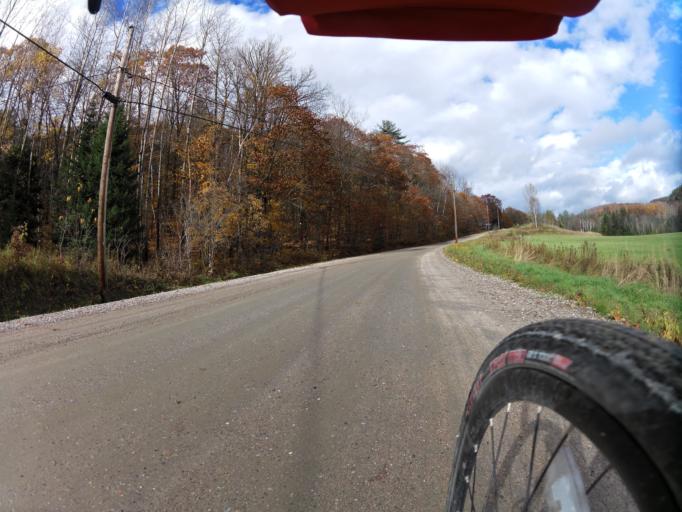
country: CA
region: Quebec
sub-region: Outaouais
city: Wakefield
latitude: 45.7020
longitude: -76.0238
